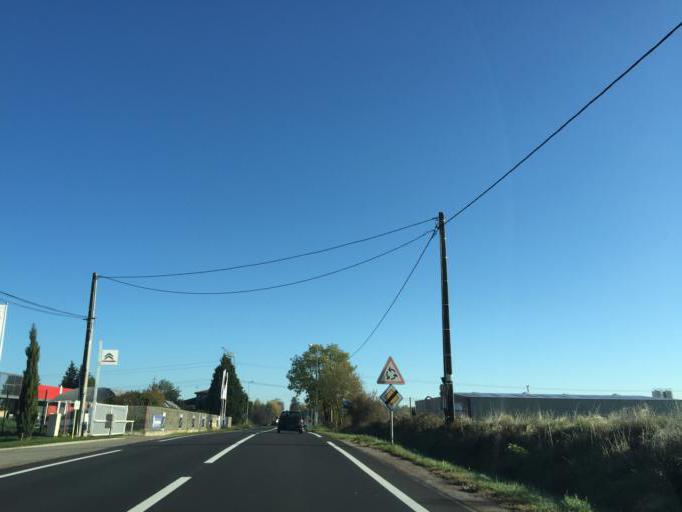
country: FR
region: Rhone-Alpes
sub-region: Departement du Rhone
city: Chassagny
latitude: 45.6171
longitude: 4.7080
